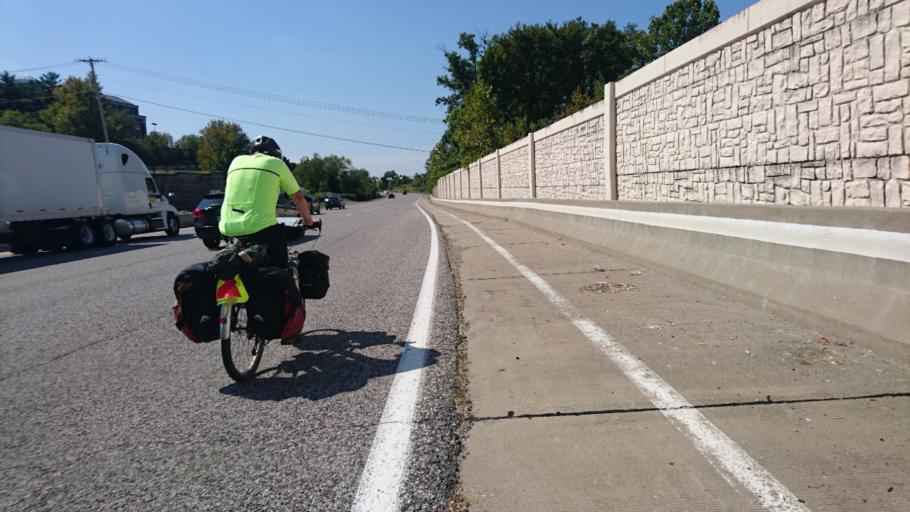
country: US
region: Missouri
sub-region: Saint Louis County
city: Town and Country
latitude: 38.6042
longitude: -90.4621
